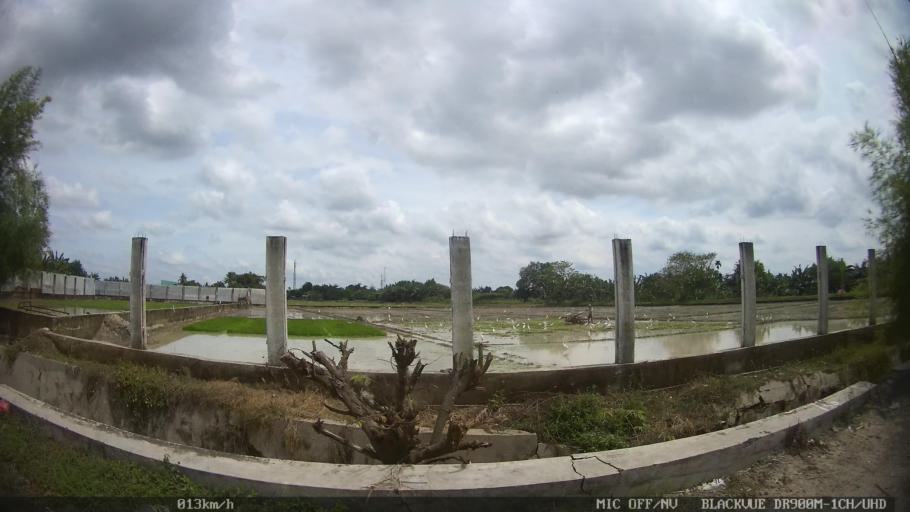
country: ID
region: North Sumatra
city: Percut
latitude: 3.5651
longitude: 98.8569
